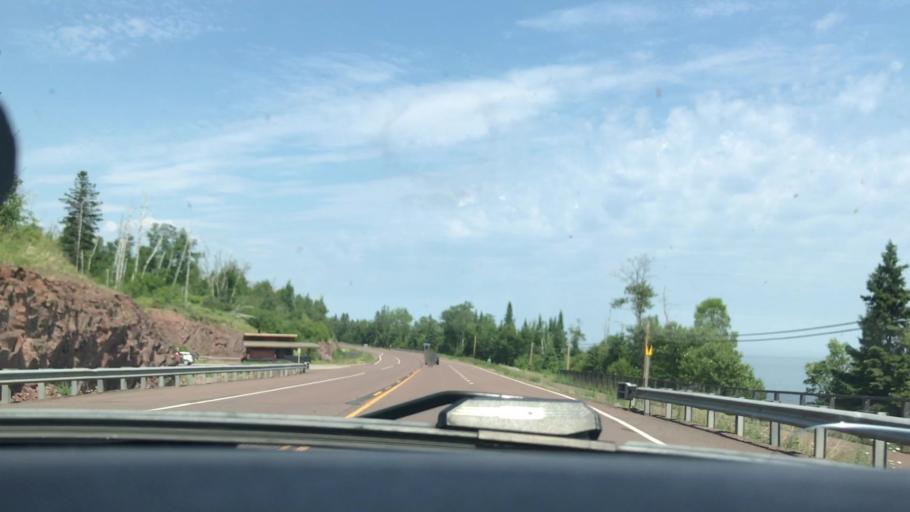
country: US
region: Minnesota
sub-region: Cook County
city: Grand Marais
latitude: 47.6086
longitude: -90.7704
